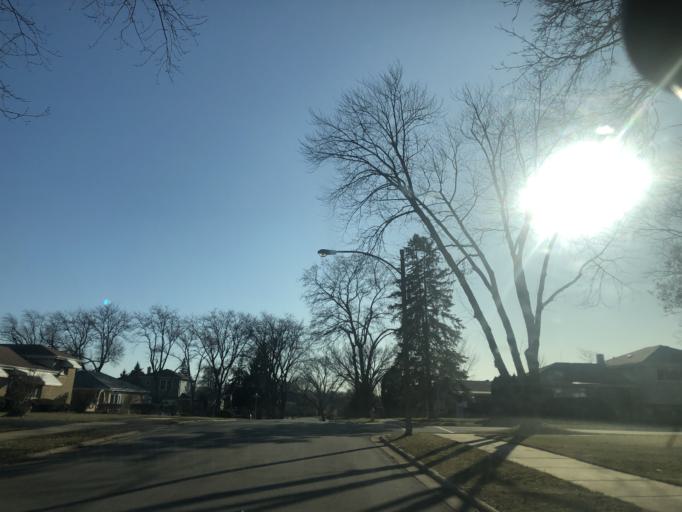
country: US
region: Illinois
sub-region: DuPage County
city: Addison
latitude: 41.9402
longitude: -87.9996
